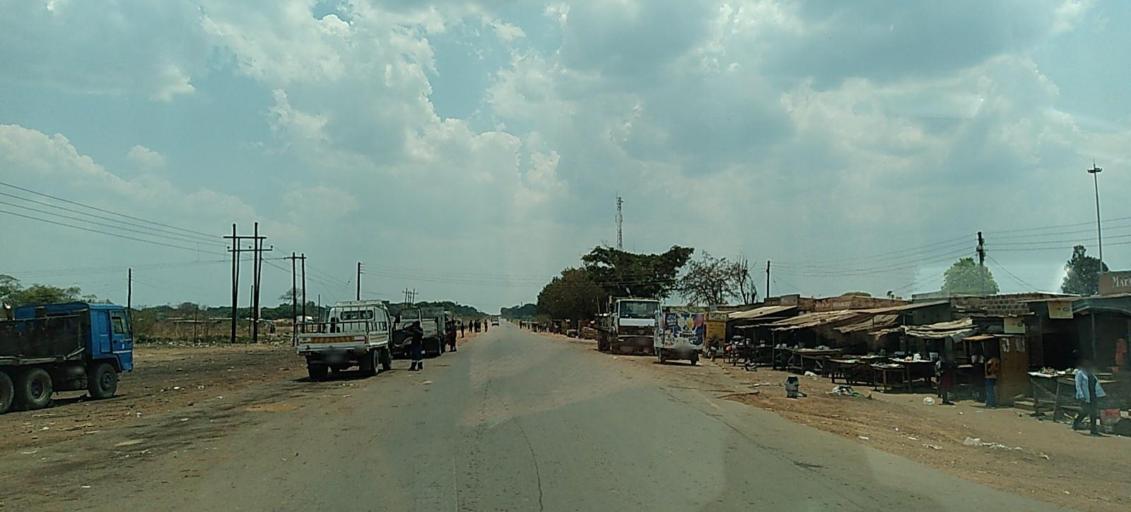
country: ZM
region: Copperbelt
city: Kalulushi
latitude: -12.8342
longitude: 27.9686
